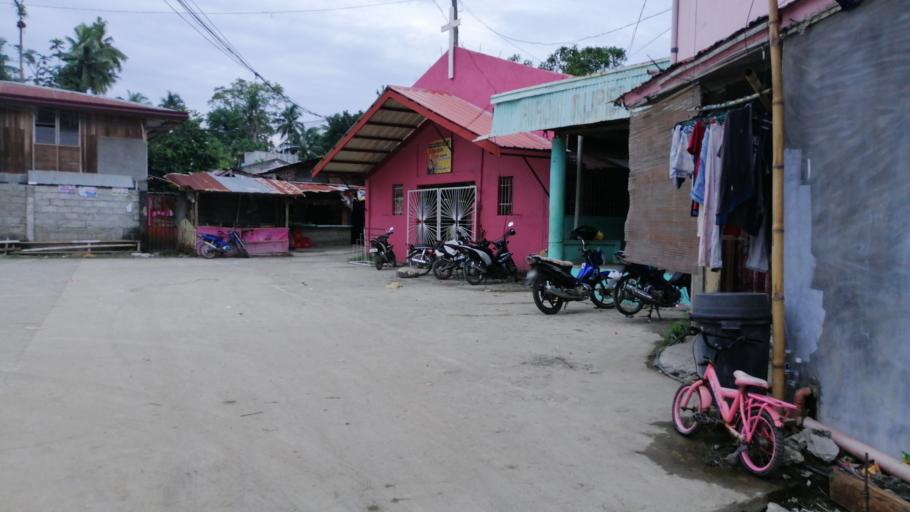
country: PH
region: Davao
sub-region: Province of Davao del Norte
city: Tagum
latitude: 7.4511
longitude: 125.8197
